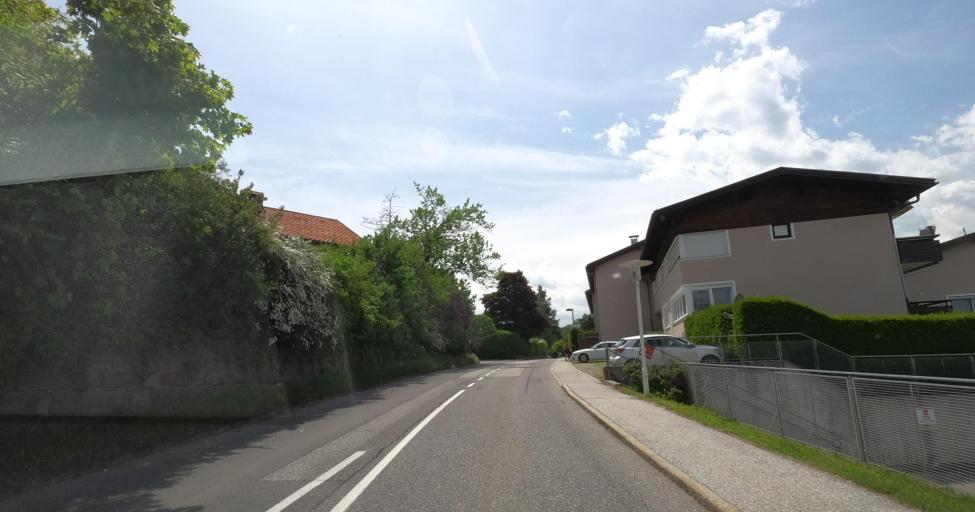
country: AT
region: Tyrol
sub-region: Politischer Bezirk Innsbruck Land
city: Sistrans
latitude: 47.2408
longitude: 11.4357
